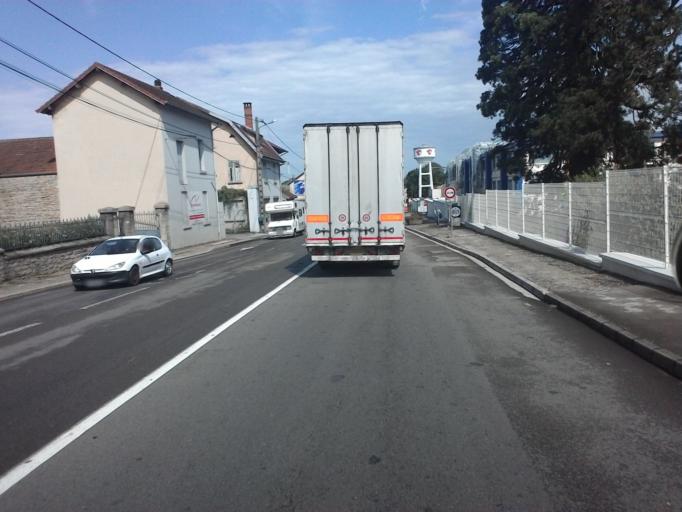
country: FR
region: Franche-Comte
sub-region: Departement du Jura
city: Lons-le-Saunier
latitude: 46.6695
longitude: 5.5470
